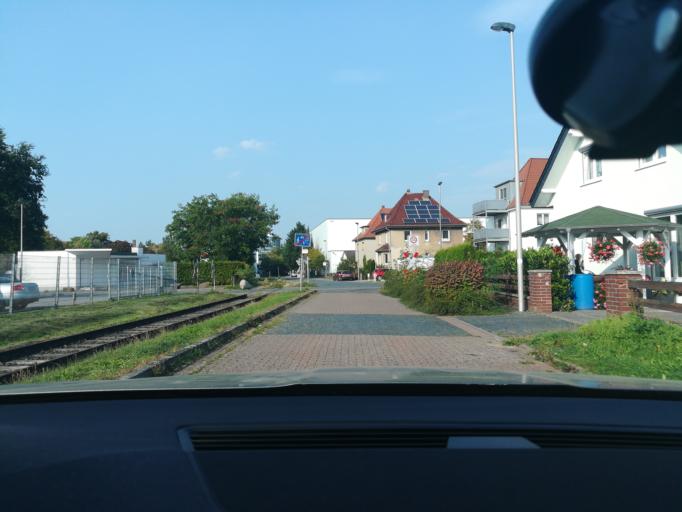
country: DE
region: North Rhine-Westphalia
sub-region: Regierungsbezirk Detmold
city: Minden
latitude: 52.2961
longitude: 8.9220
